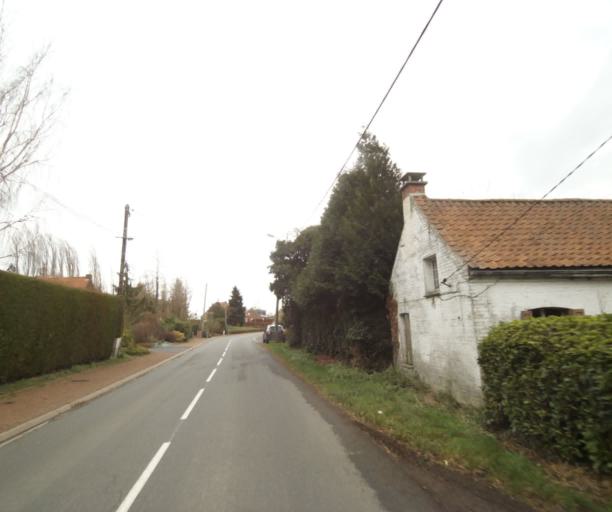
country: FR
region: Nord-Pas-de-Calais
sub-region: Departement du Nord
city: Sebourg
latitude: 50.3328
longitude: 3.6570
